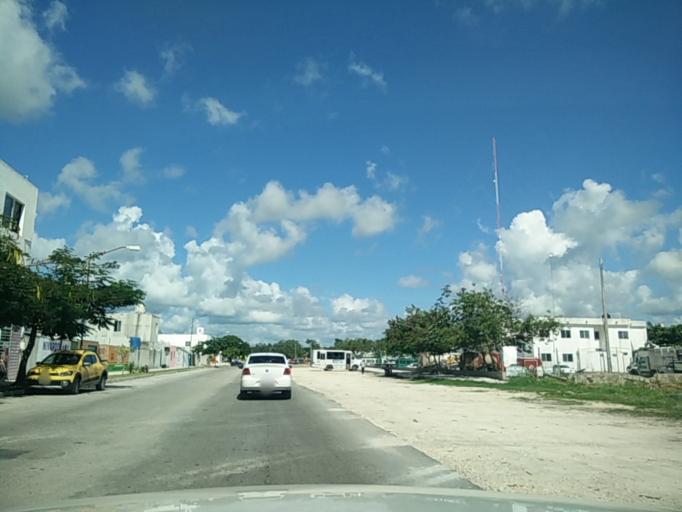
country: MX
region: Quintana Roo
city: Playa del Carmen
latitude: 20.6648
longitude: -87.0651
